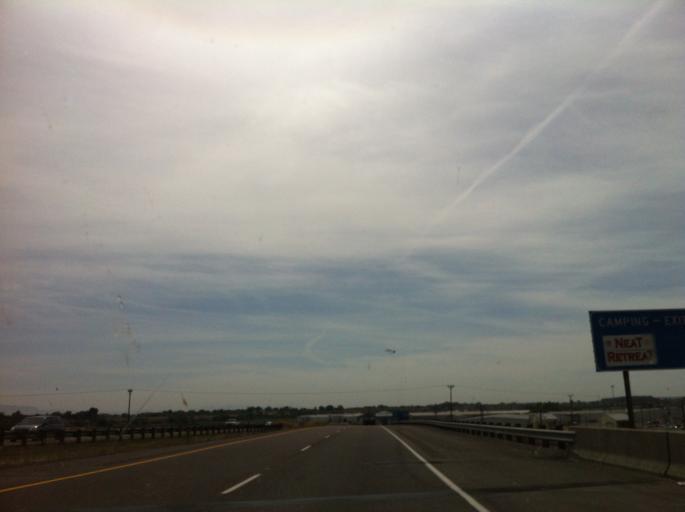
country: US
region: Oregon
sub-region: Malheur County
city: Ontario
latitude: 44.0363
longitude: -116.9598
